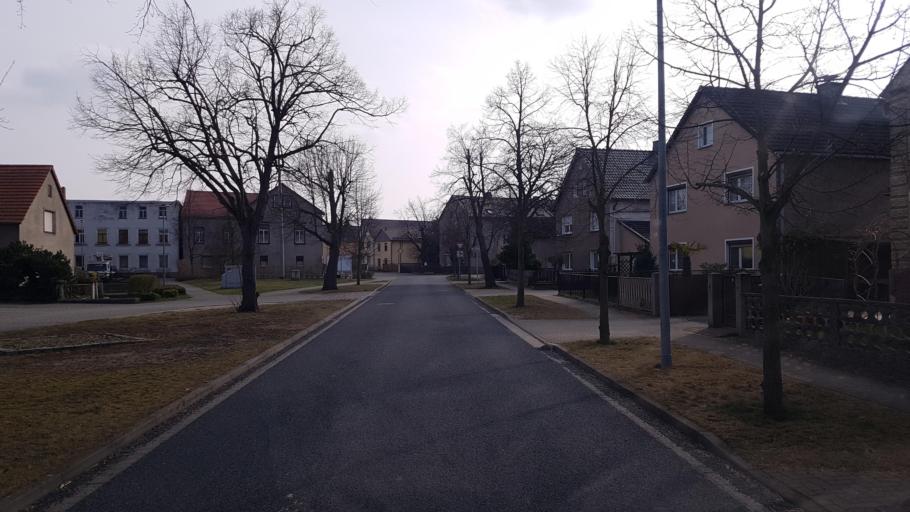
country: DE
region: Brandenburg
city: Merzdorf
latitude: 51.4046
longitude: 13.5341
